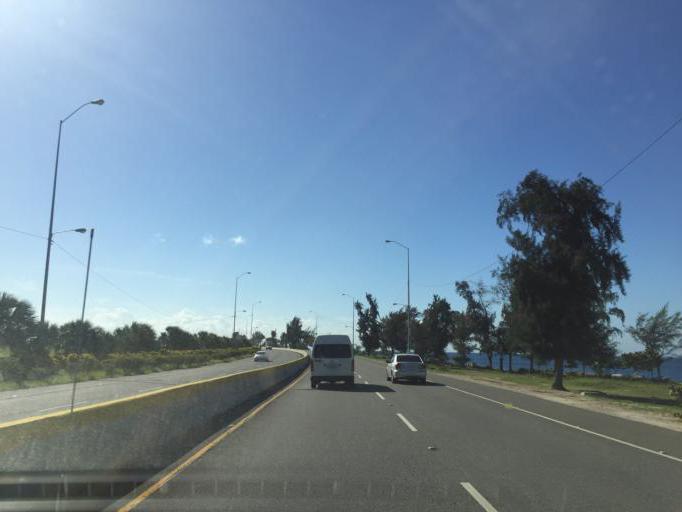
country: DO
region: Santo Domingo
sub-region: Santo Domingo
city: Boca Chica
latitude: 18.4427
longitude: -69.6813
